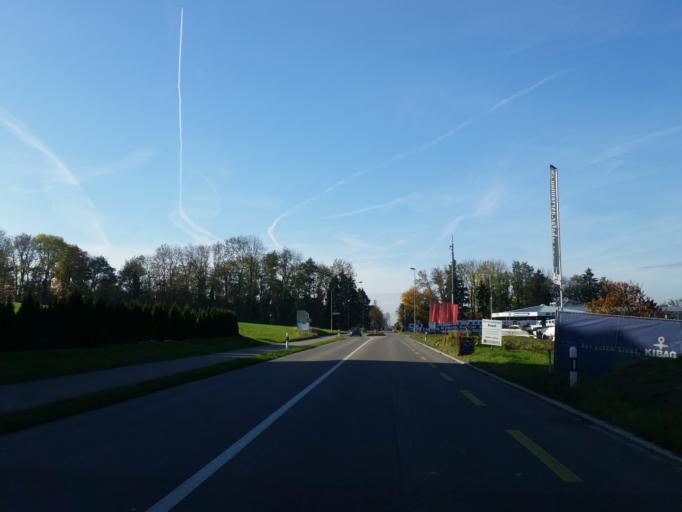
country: CH
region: Thurgau
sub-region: Arbon District
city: Uttwil
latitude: 47.5857
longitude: 9.3365
